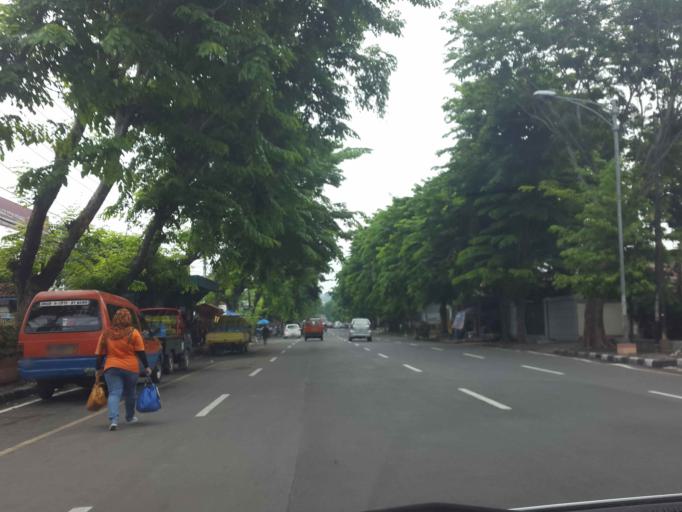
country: ID
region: Central Java
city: Semarang
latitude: -6.9961
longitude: 110.4338
